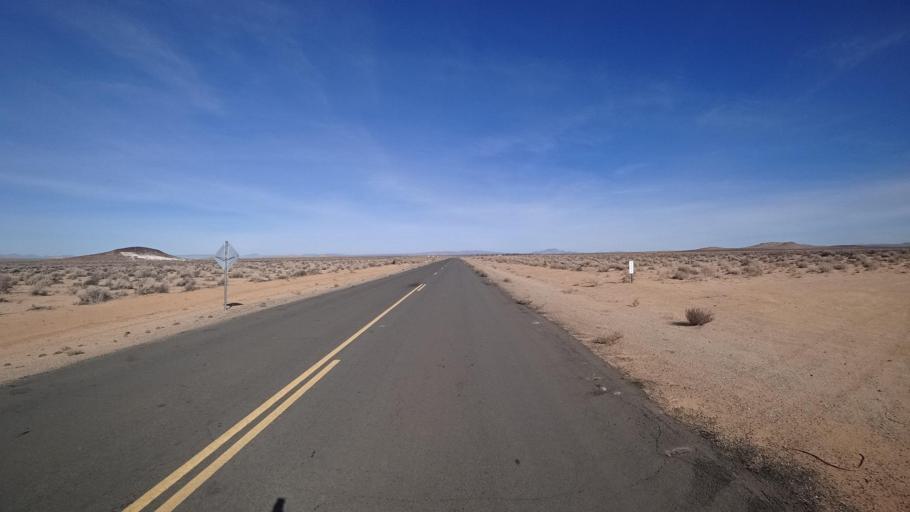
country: US
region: California
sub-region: Kern County
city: North Edwards
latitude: 35.0652
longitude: -117.8048
